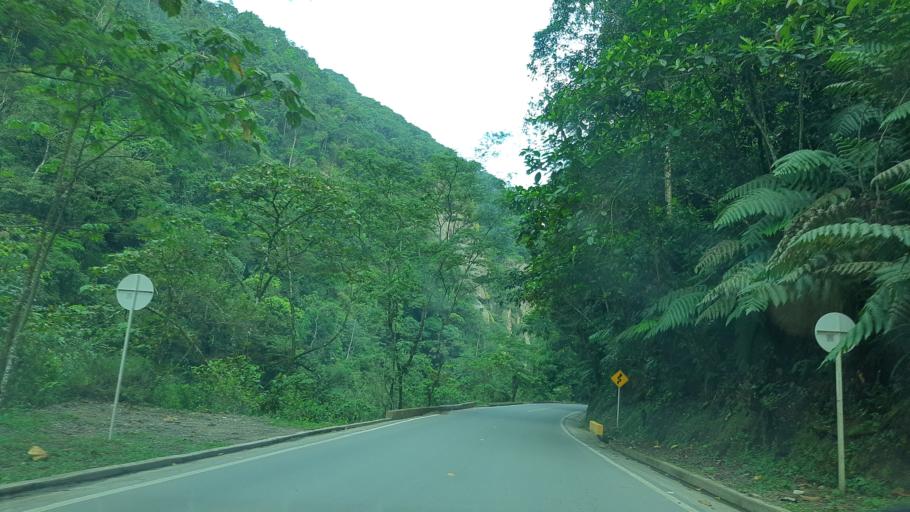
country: CO
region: Boyaca
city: Santa Maria
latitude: 4.8508
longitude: -73.2290
